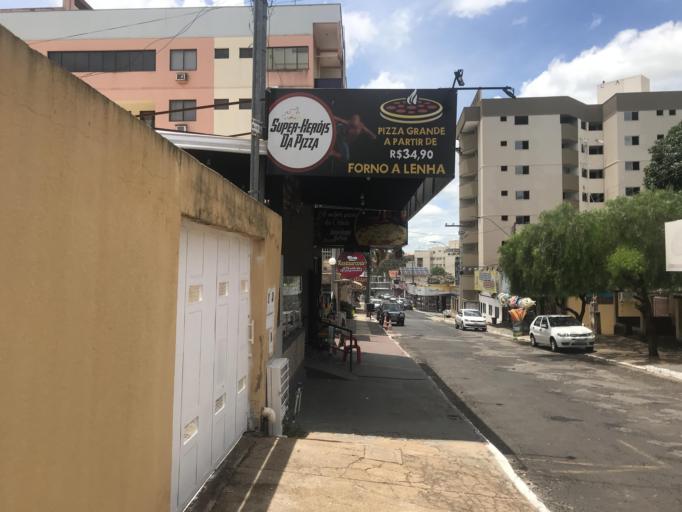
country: BR
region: Goias
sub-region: Caldas Novas
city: Caldas Novas
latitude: -17.7693
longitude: -48.7553
